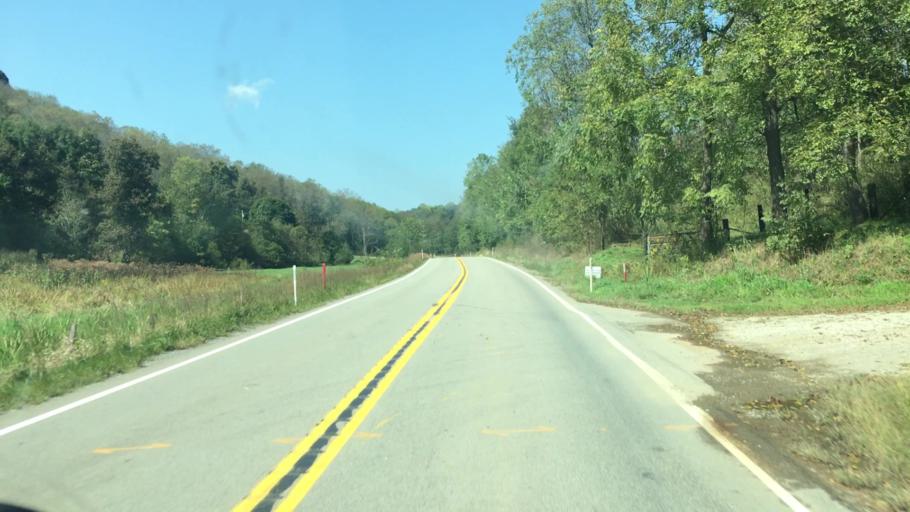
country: US
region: Pennsylvania
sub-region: Greene County
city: Waynesburg
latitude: 39.9719
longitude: -80.3209
